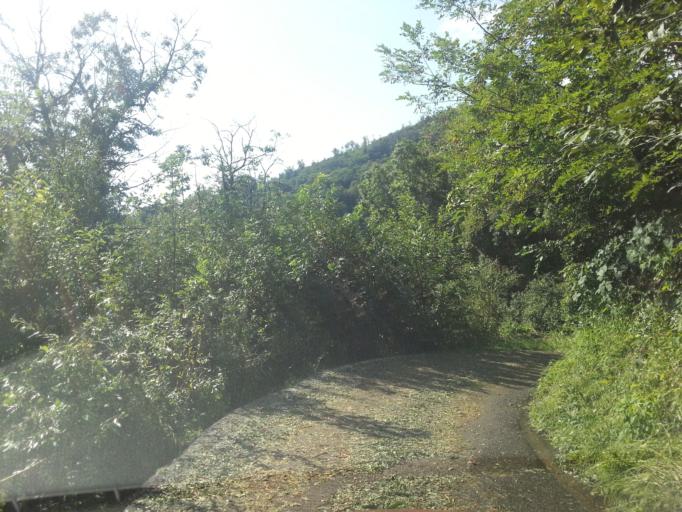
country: IT
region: Lombardy
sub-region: Provincia di Lecco
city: Santa Maria Hoe
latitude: 45.7529
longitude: 9.3958
